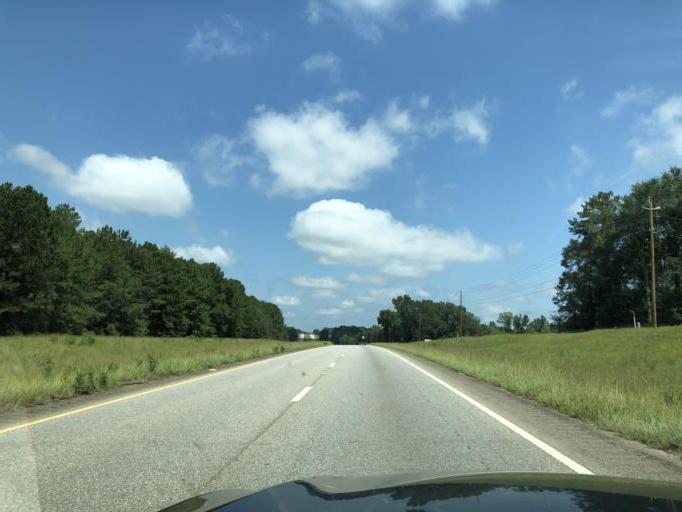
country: US
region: Alabama
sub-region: Henry County
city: Abbeville
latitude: 31.5605
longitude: -85.2812
